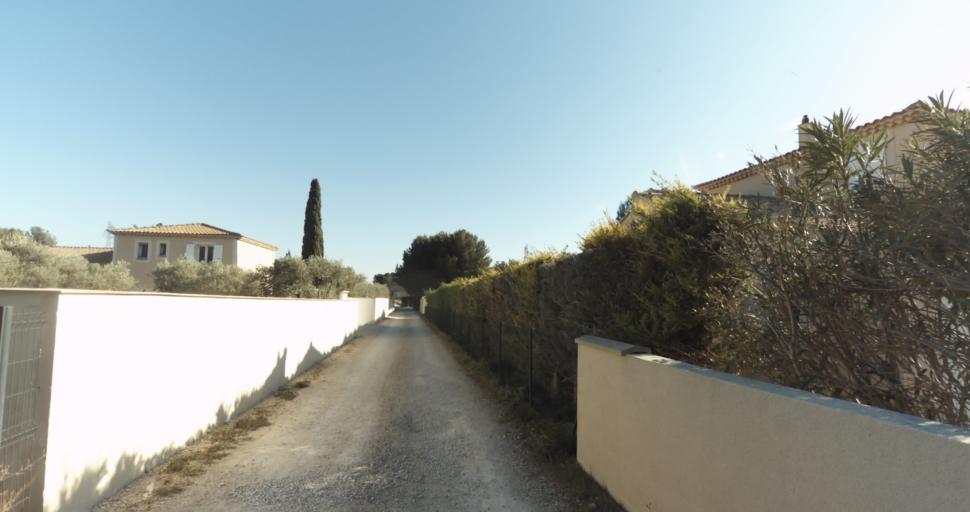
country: FR
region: Provence-Alpes-Cote d'Azur
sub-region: Departement des Bouches-du-Rhone
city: Pelissanne
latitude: 43.6419
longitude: 5.1485
